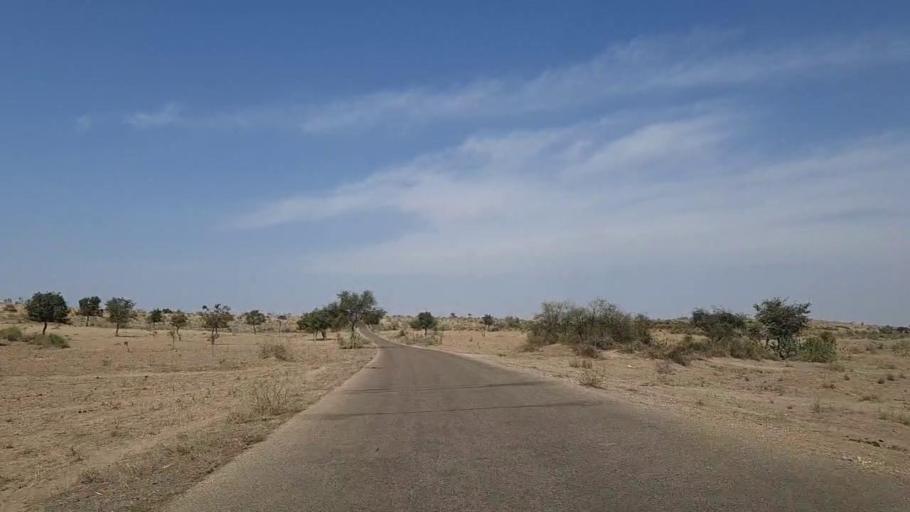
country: PK
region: Sindh
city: Umarkot
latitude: 25.1419
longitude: 70.0128
